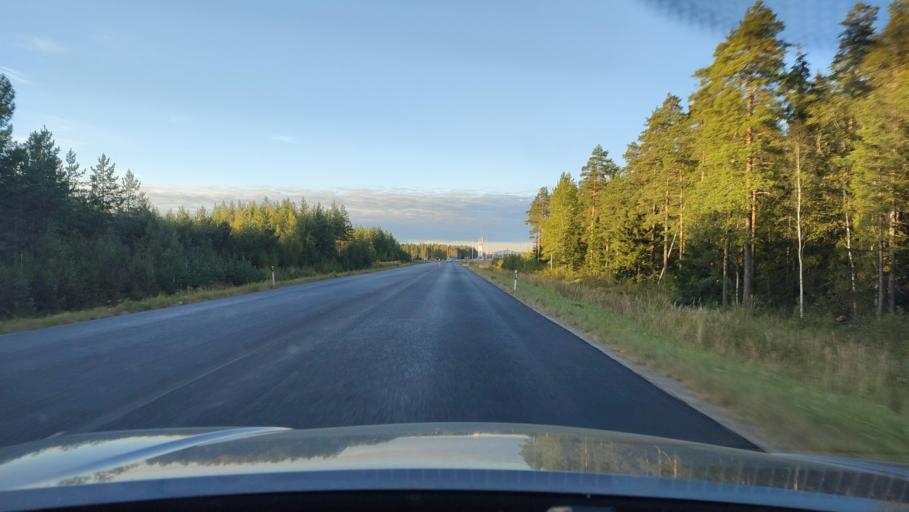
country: FI
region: Ostrobothnia
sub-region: Sydosterbotten
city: Kristinestad
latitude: 62.2225
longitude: 21.5215
